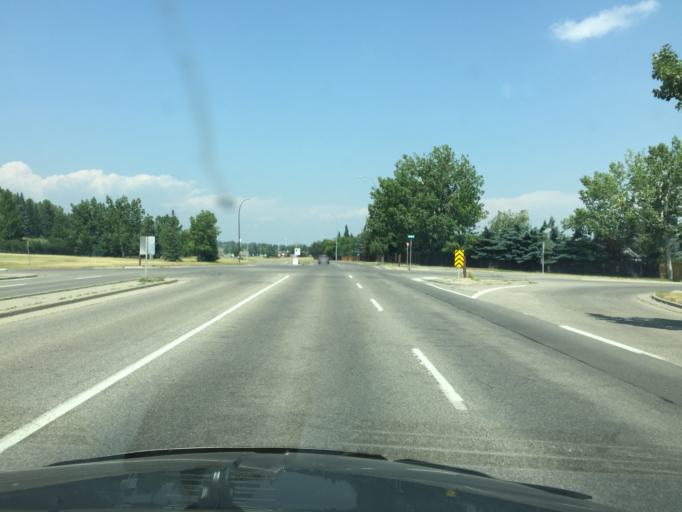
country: CA
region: Alberta
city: Calgary
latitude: 50.9180
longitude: -114.0183
